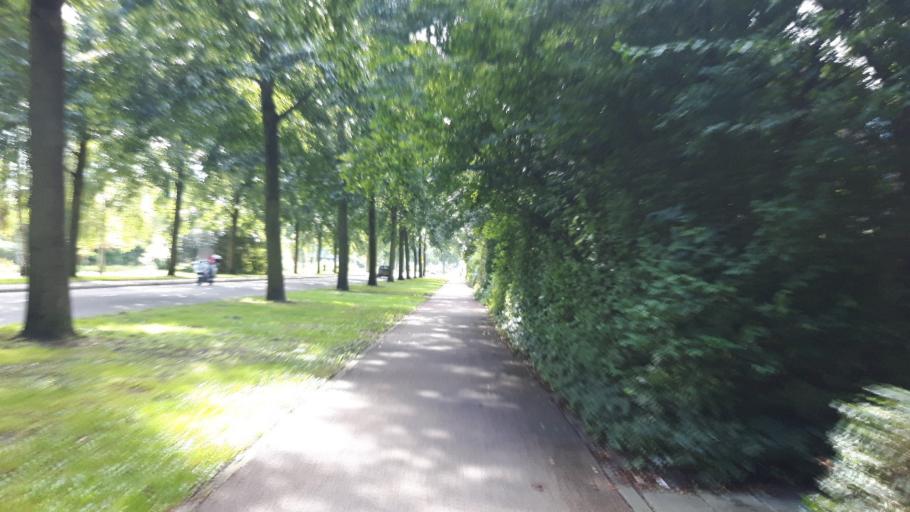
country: NL
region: North Holland
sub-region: Gemeente Purmerend
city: Purmerend
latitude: 52.5146
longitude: 4.9566
